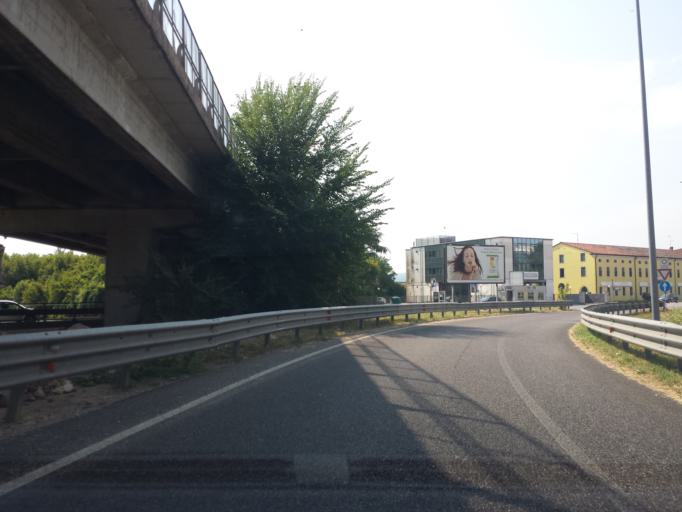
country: IT
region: Veneto
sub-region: Provincia di Vicenza
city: Creazzo
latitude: 45.5350
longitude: 11.5078
